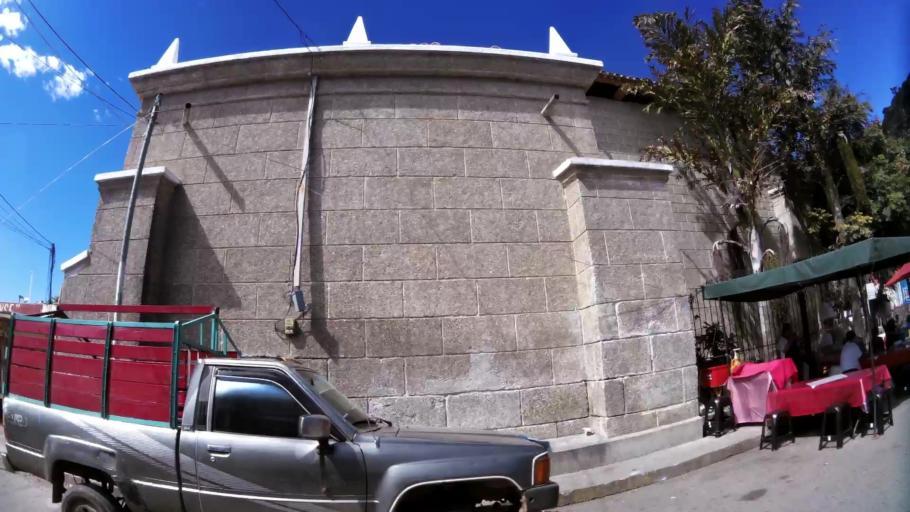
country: GT
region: Solola
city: Panajachel
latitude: 14.7457
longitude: -91.1530
